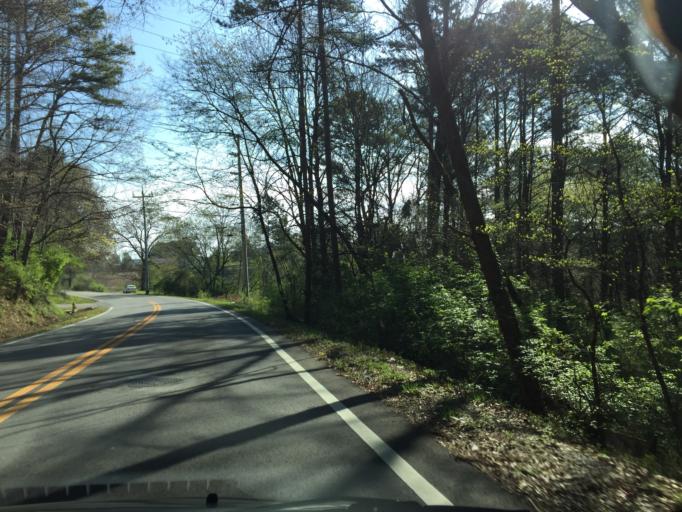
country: US
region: Tennessee
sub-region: Hamilton County
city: East Chattanooga
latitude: 35.0688
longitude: -85.2102
